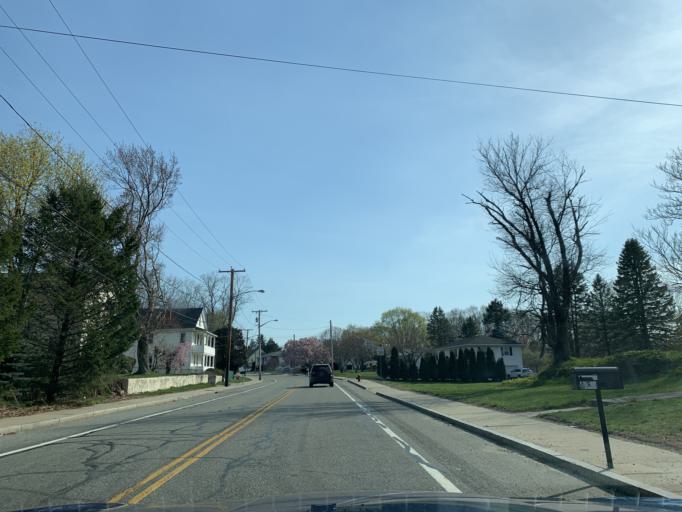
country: US
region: Rhode Island
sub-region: Providence County
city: Johnston
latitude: 41.7960
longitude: -71.5062
